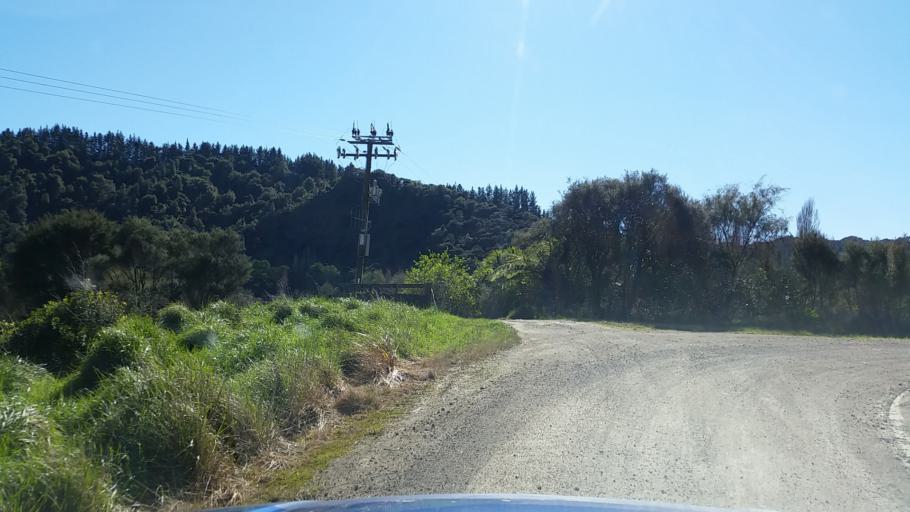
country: NZ
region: Manawatu-Wanganui
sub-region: Wanganui District
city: Wanganui
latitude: -39.6675
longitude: 174.8609
